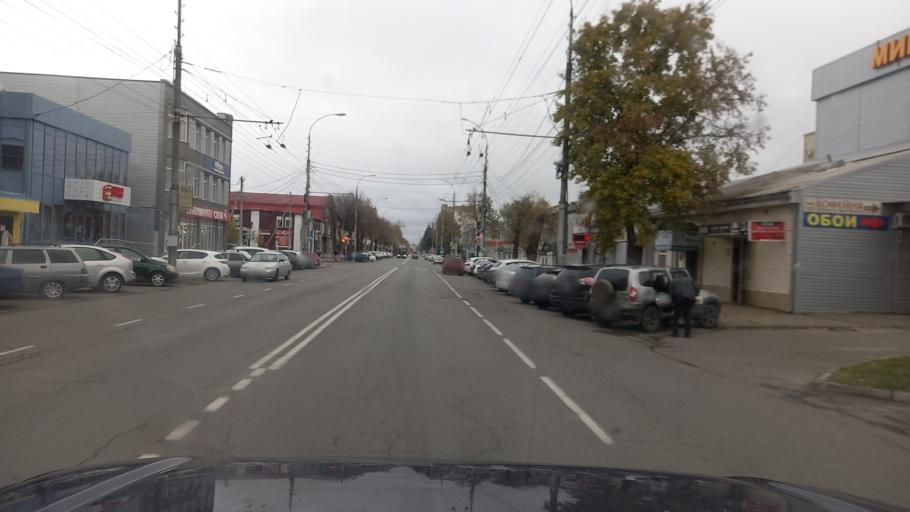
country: RU
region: Adygeya
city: Maykop
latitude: 44.6098
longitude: 40.1076
